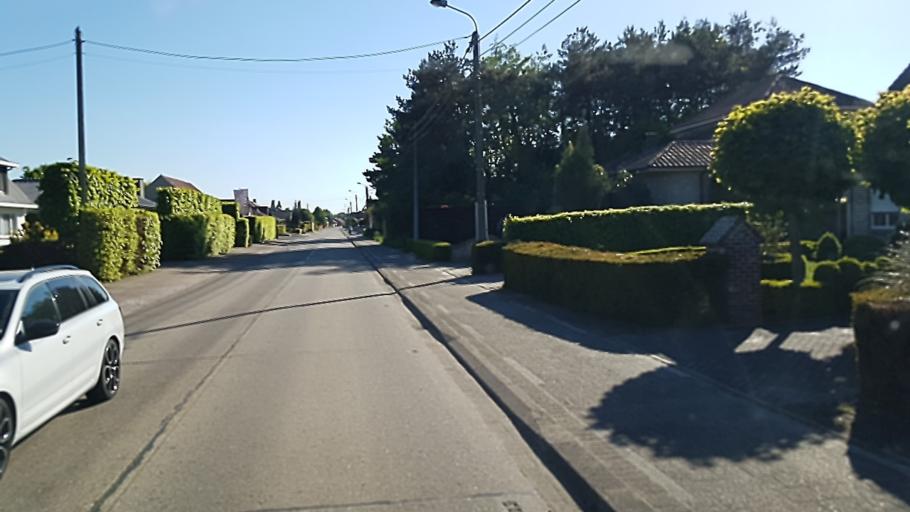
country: BE
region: Flanders
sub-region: Provincie Antwerpen
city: Berlaar
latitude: 51.0868
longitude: 4.6827
